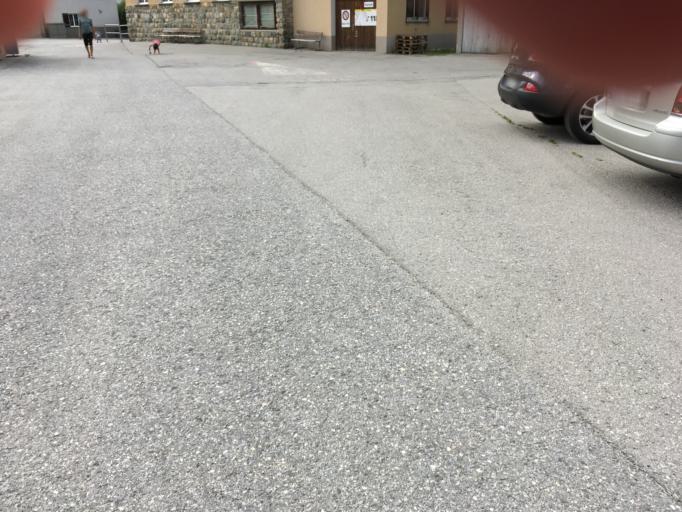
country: CH
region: Grisons
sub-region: Maloja District
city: Silvaplana
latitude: 46.4679
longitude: 9.6520
